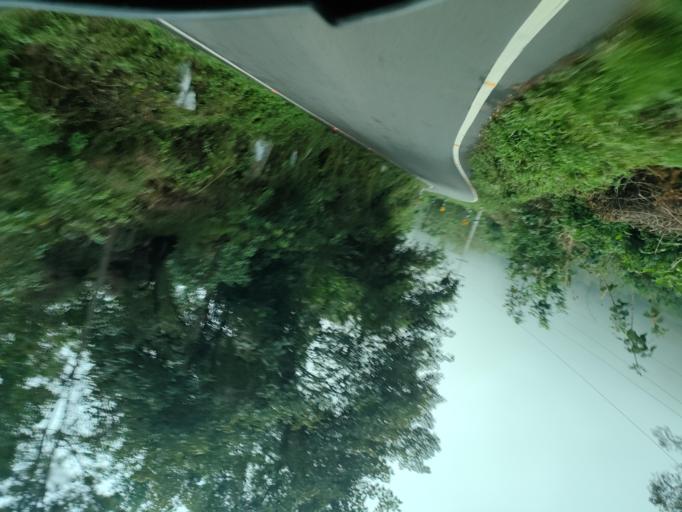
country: IN
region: Tamil Nadu
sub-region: Dindigul
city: Ayakudi
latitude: 10.3554
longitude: 77.5592
